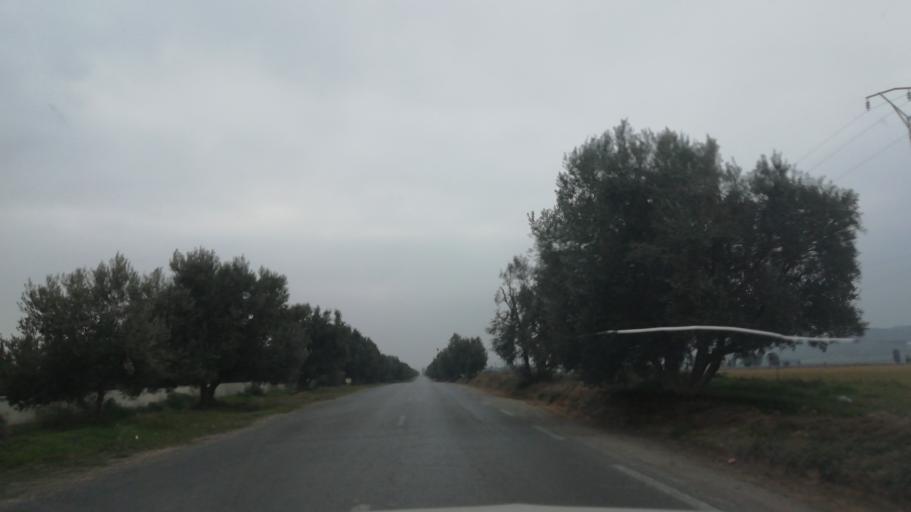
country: DZ
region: Sidi Bel Abbes
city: Sfizef
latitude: 35.2268
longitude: -0.2710
